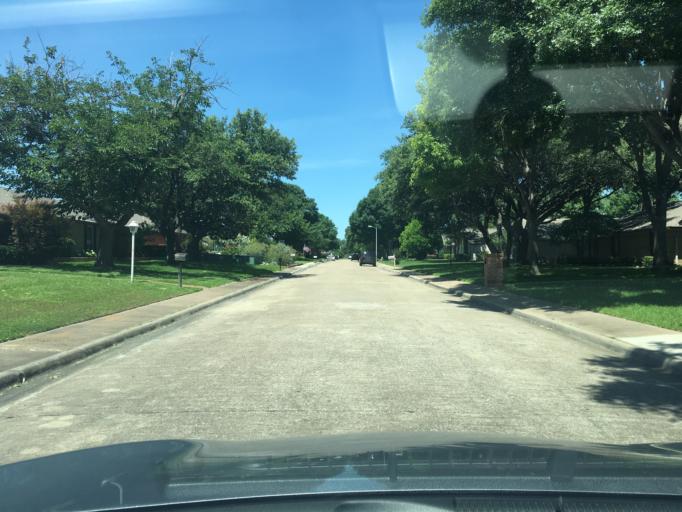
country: US
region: Texas
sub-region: Dallas County
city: Richardson
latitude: 32.9476
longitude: -96.6926
